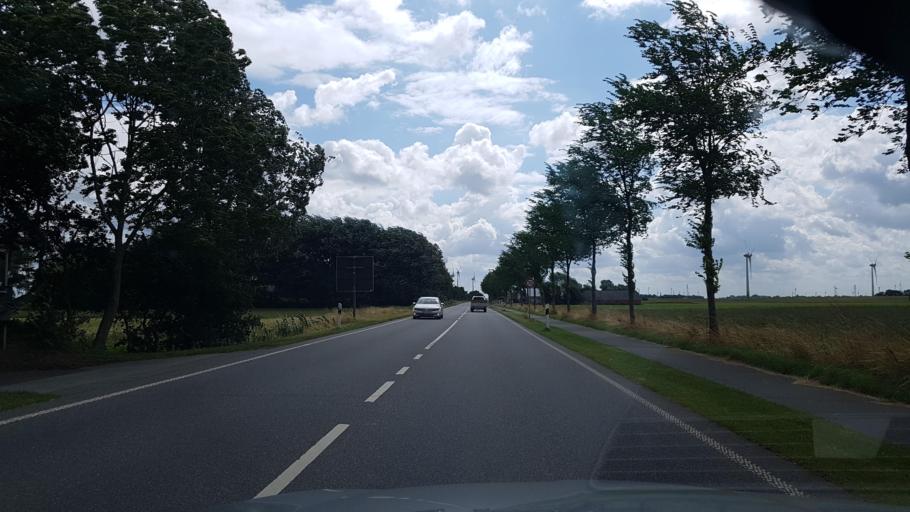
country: DE
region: Schleswig-Holstein
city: Wesselburenerkoog
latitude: 54.2386
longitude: 8.8791
